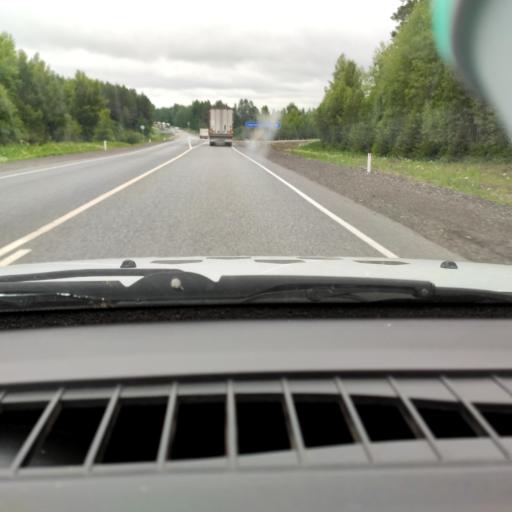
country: RU
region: Udmurtiya
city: Alnashi
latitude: 56.0990
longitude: 52.4552
